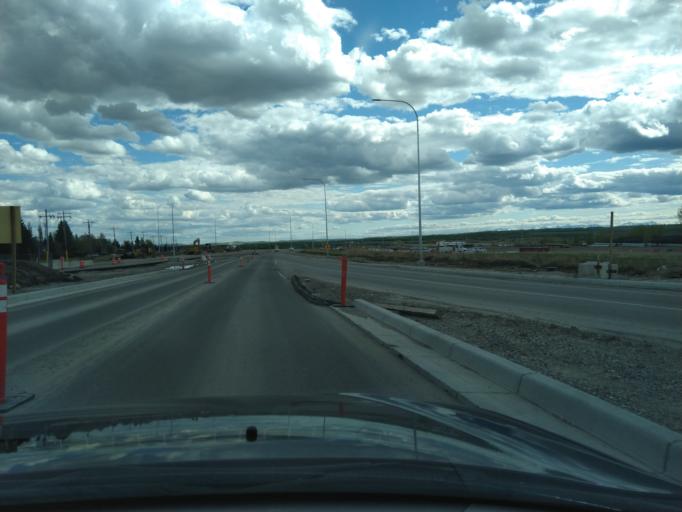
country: CA
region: Alberta
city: Calgary
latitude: 51.0075
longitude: -114.1418
